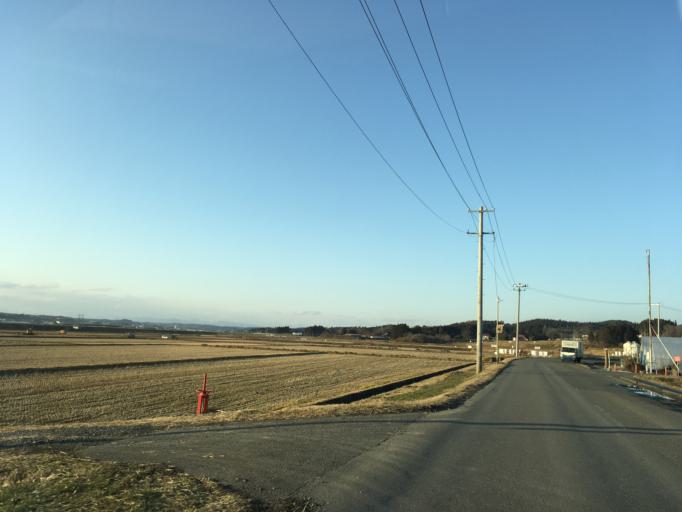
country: JP
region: Iwate
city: Ichinoseki
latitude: 38.8123
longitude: 141.2140
